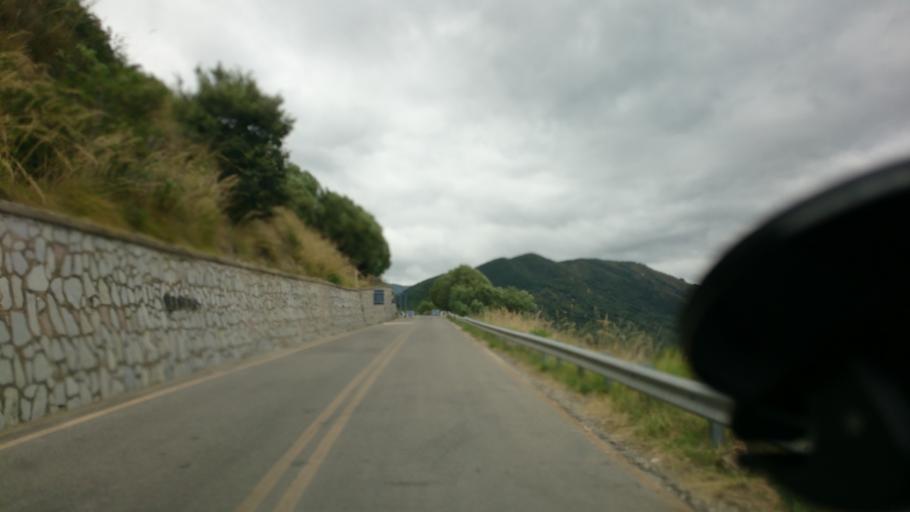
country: IT
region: Campania
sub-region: Provincia di Salerno
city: Ascea
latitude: 40.1271
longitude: 15.1993
